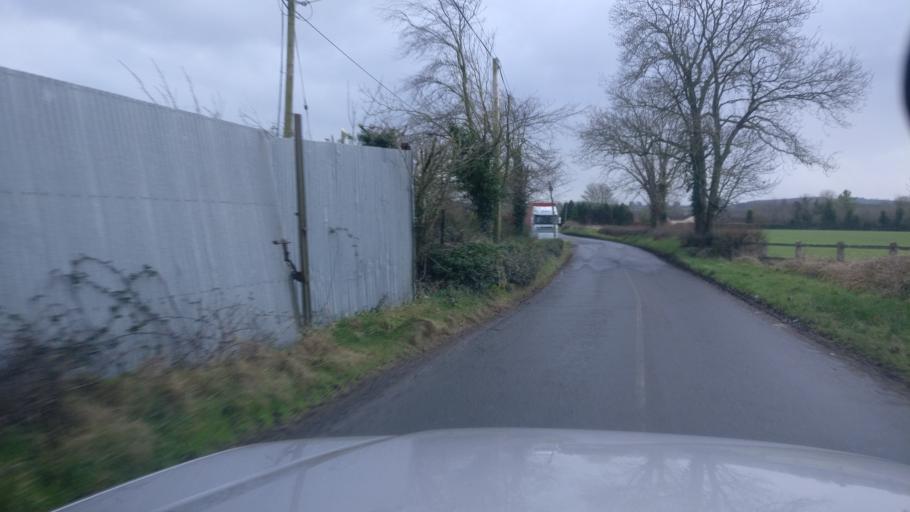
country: IE
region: Munster
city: Nenagh Bridge
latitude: 52.9876
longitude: -8.1135
